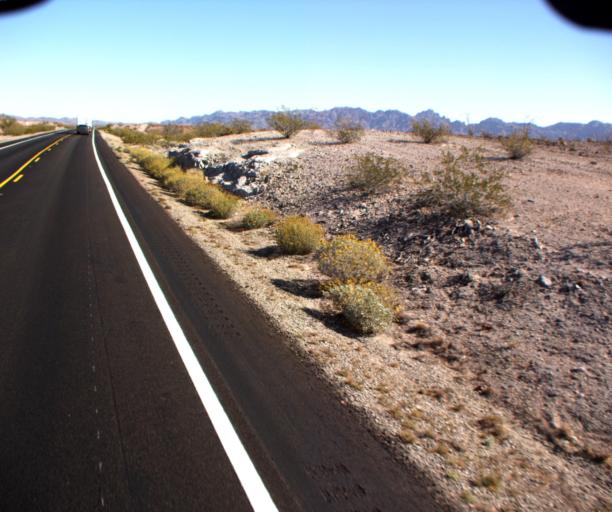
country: US
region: Arizona
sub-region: Yuma County
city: Wellton
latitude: 33.1027
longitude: -114.2977
